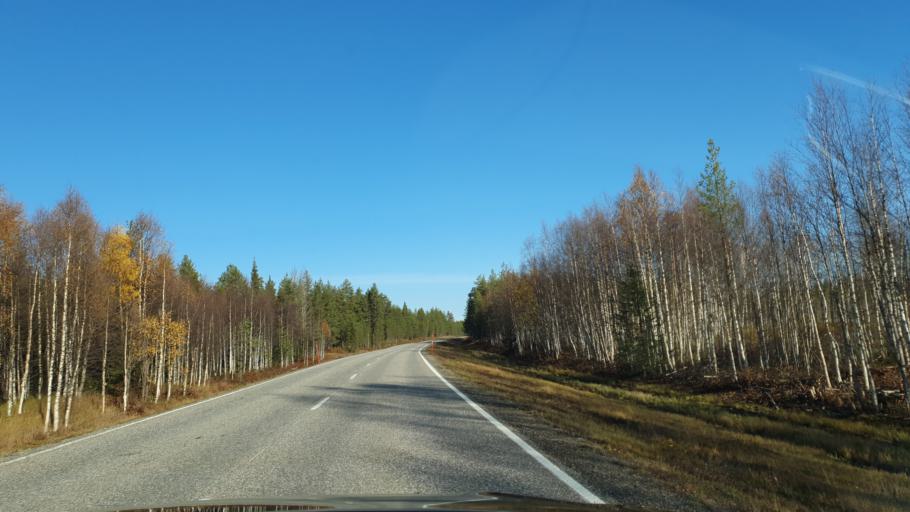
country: FI
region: Lapland
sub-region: Tunturi-Lappi
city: Kittilae
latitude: 67.3983
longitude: 24.9143
